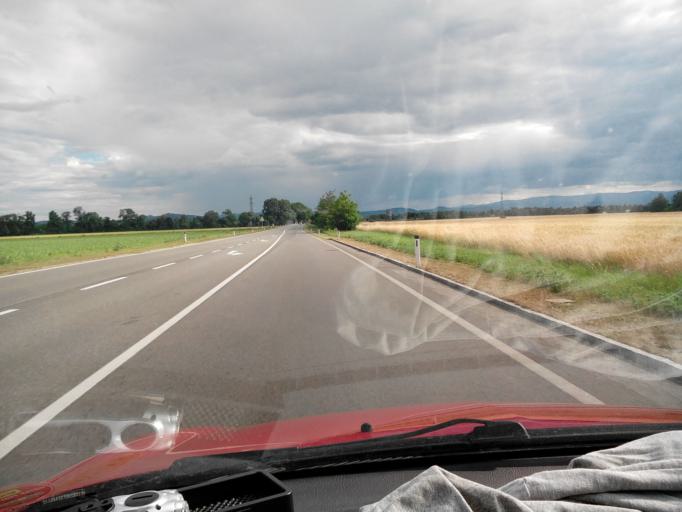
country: AT
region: Lower Austria
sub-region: Wiener Neustadt Stadt
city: Wiener Neustadt
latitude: 47.7943
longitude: 16.2376
